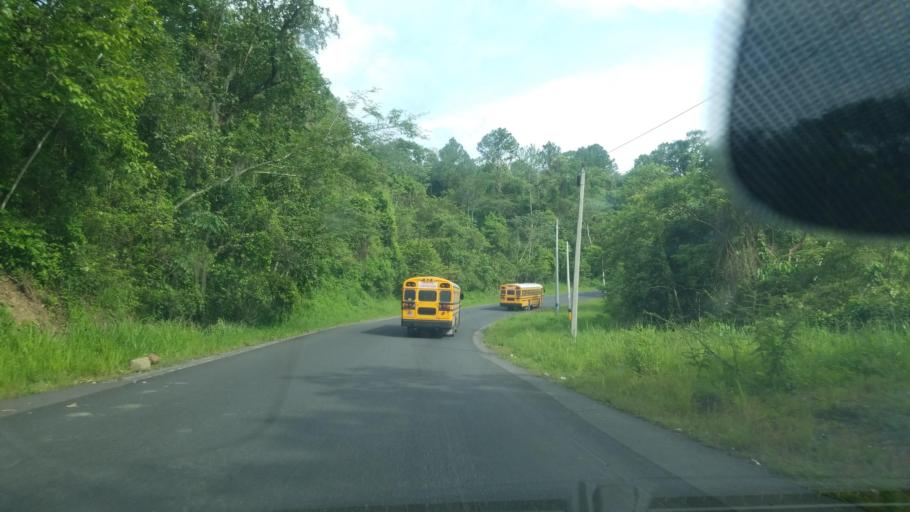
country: HN
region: Santa Barbara
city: Petoa
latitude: 15.2007
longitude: -88.2705
